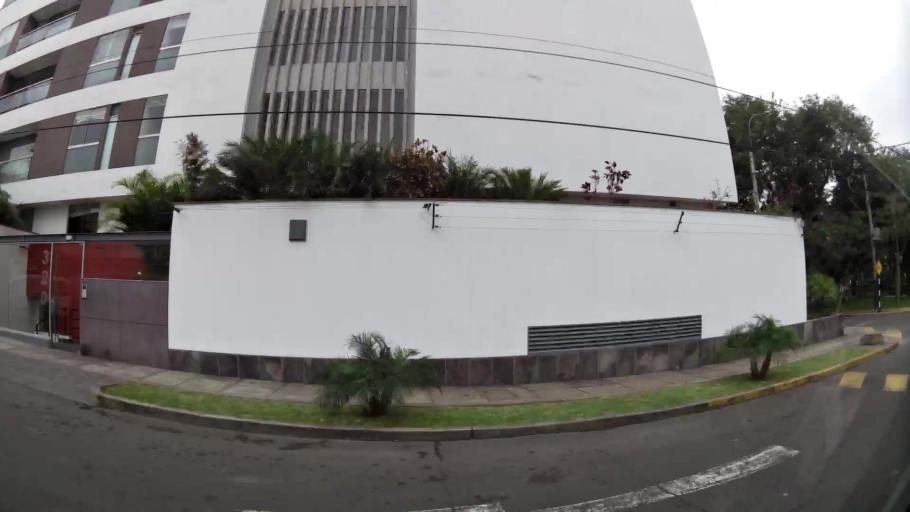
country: PE
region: Lima
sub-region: Lima
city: Surco
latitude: -12.1191
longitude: -77.0094
